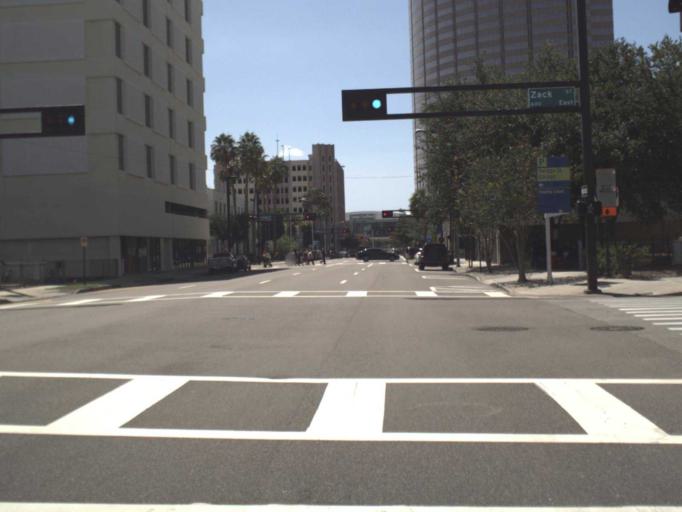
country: US
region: Florida
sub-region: Hillsborough County
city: Tampa
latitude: 27.9512
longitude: -82.4557
